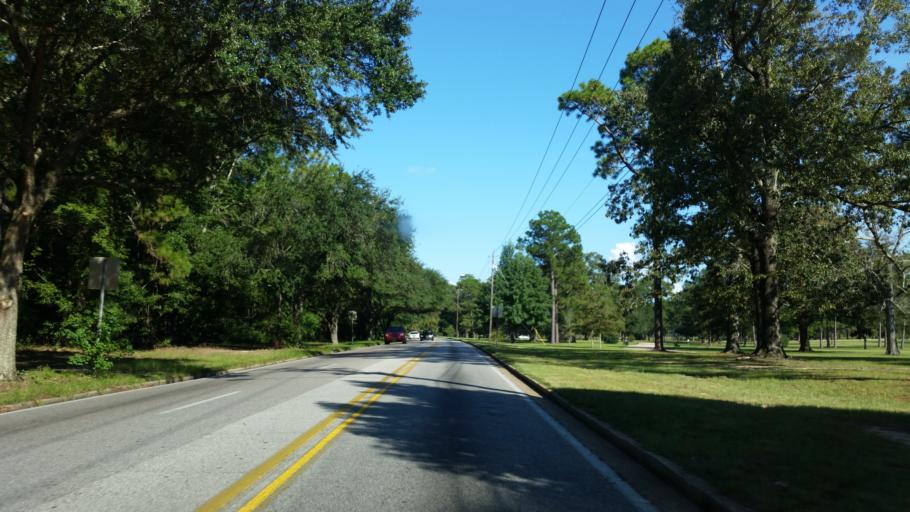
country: US
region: Alabama
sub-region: Mobile County
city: Prichard
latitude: 30.7103
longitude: -88.1613
